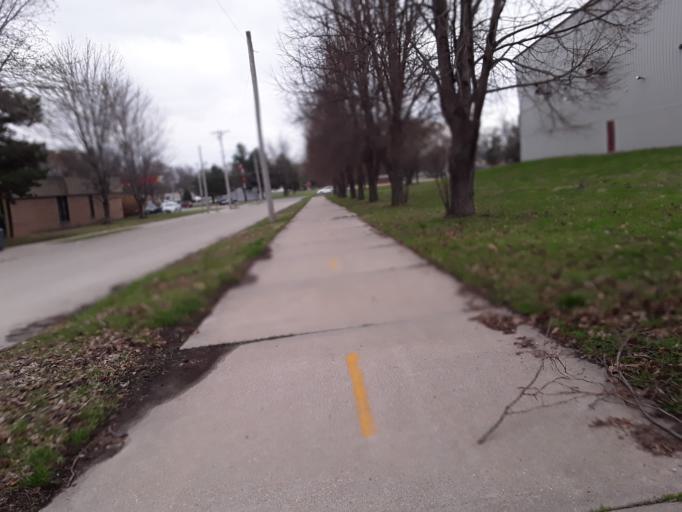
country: US
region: Nebraska
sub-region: Lancaster County
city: Lincoln
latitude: 40.8438
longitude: -96.6646
